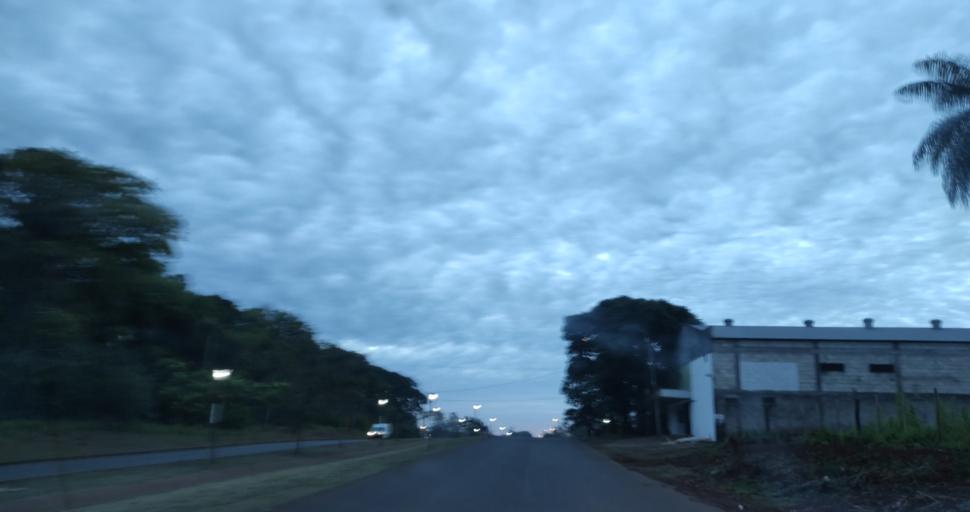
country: AR
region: Misiones
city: Garupa
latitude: -27.4679
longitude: -55.8507
